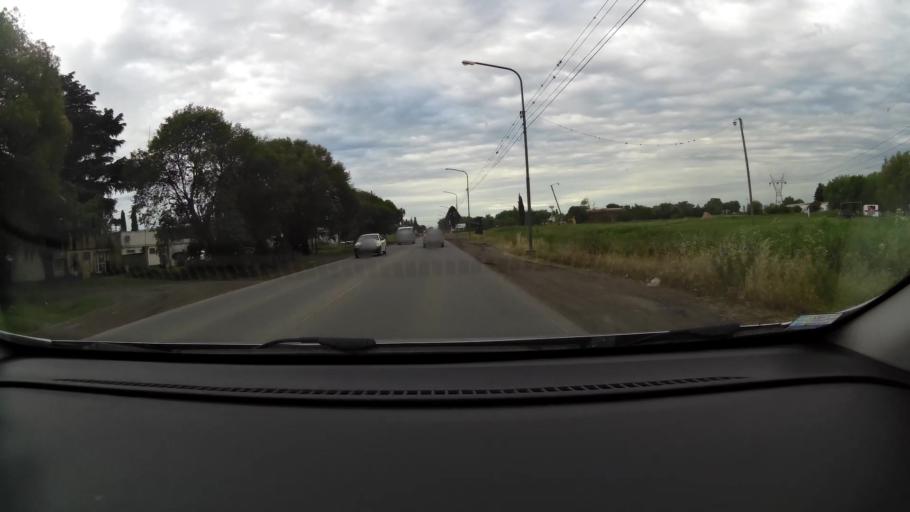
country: AR
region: Buenos Aires
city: San Nicolas de los Arroyos
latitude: -33.3732
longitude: -60.2037
